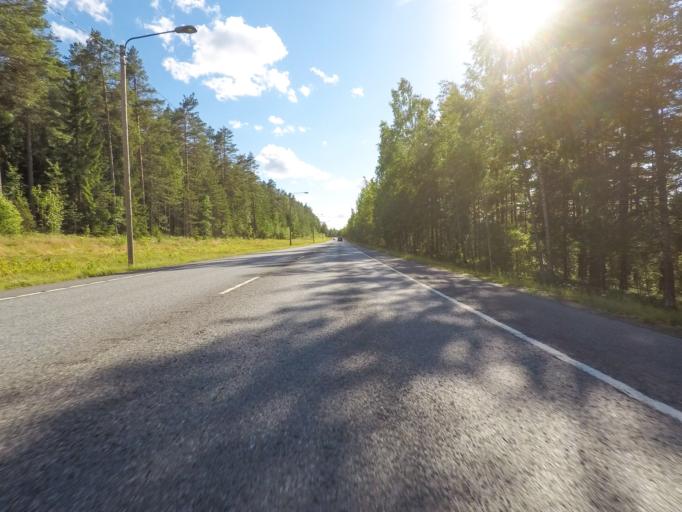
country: FI
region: Uusimaa
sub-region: Helsinki
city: Vihti
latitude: 60.3396
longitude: 24.2998
